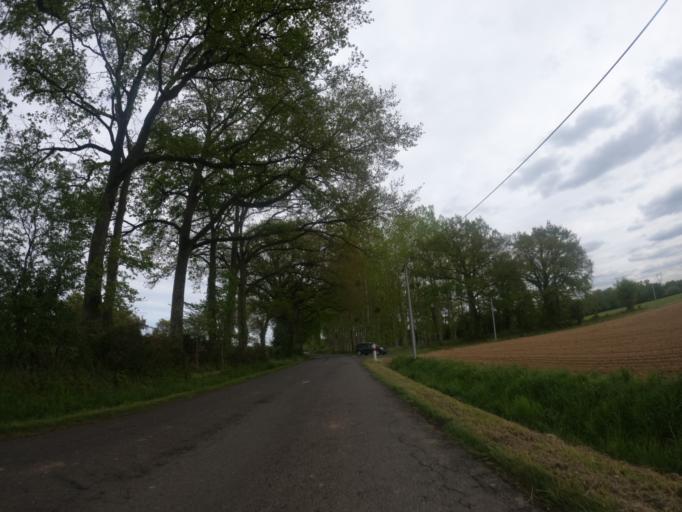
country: FR
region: Pays de la Loire
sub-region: Departement de la Loire-Atlantique
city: Rouge
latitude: 47.7378
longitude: -1.4313
